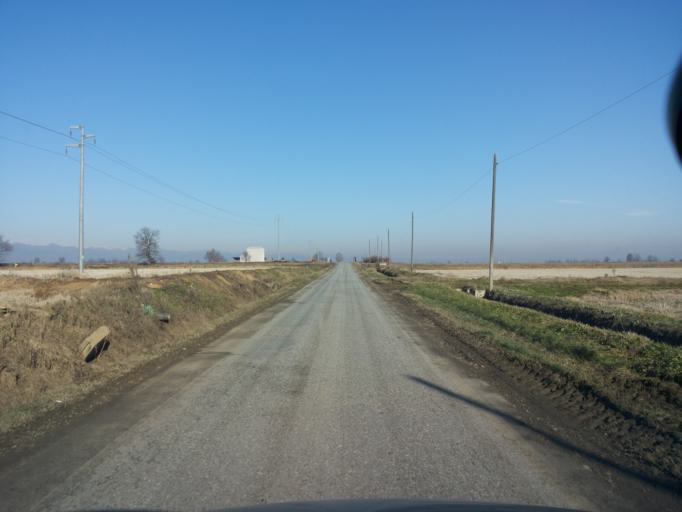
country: IT
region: Piedmont
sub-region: Provincia di Vercelli
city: Formigliana
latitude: 45.4158
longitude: 8.2501
